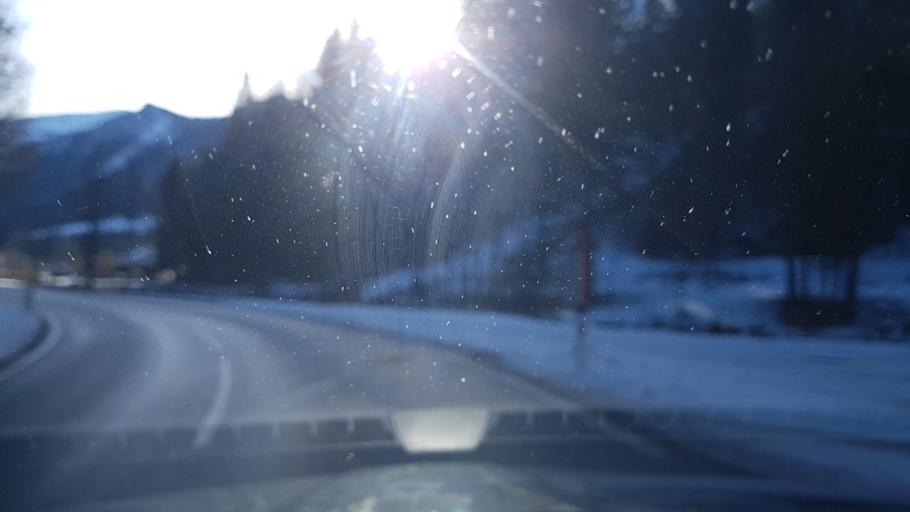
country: AT
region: Salzburg
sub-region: Politischer Bezirk Hallein
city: Krispl
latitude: 47.7160
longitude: 13.1918
